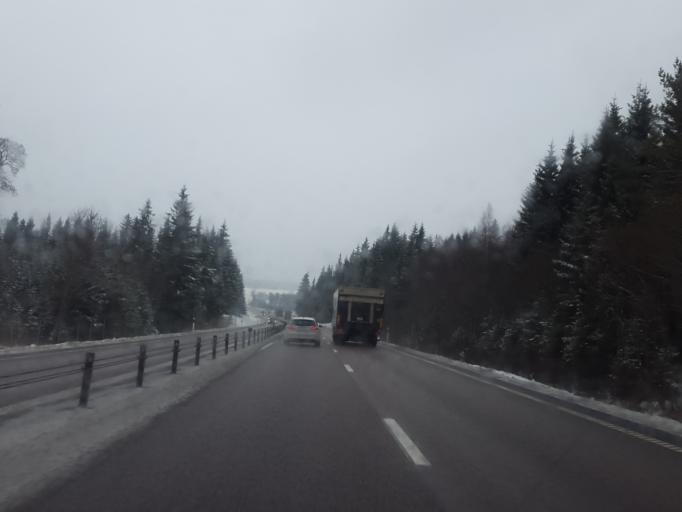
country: SE
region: Vaestra Goetaland
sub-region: Ulricehamns Kommun
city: Ulricehamn
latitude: 57.7955
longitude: 13.6155
